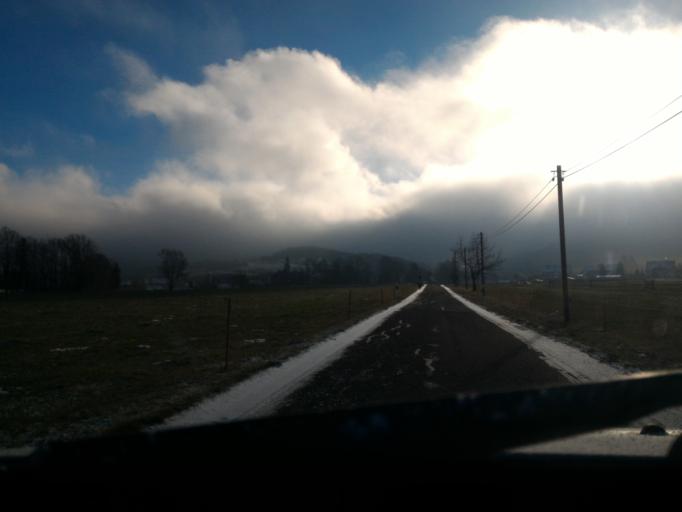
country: DE
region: Saxony
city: Grossschonau
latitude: 50.8743
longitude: 14.6458
